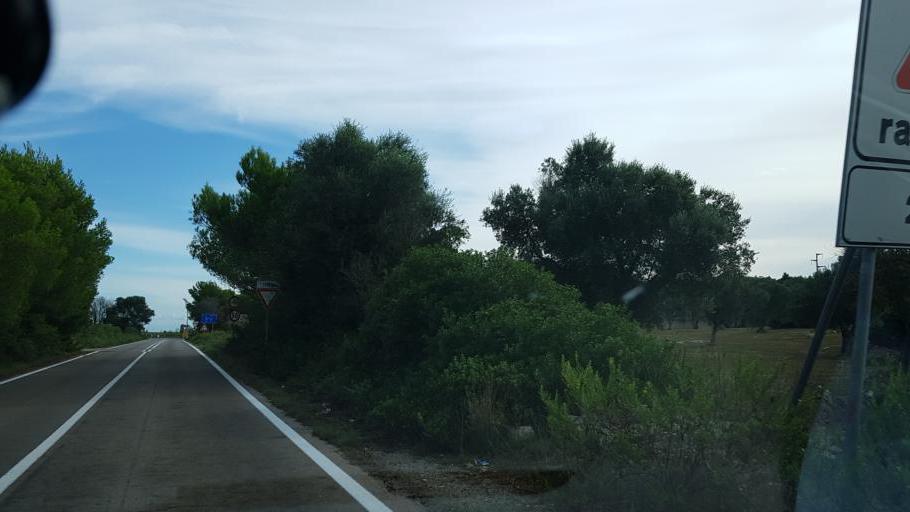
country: IT
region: Apulia
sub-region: Provincia di Lecce
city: Melendugno
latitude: 40.3380
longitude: 18.3532
